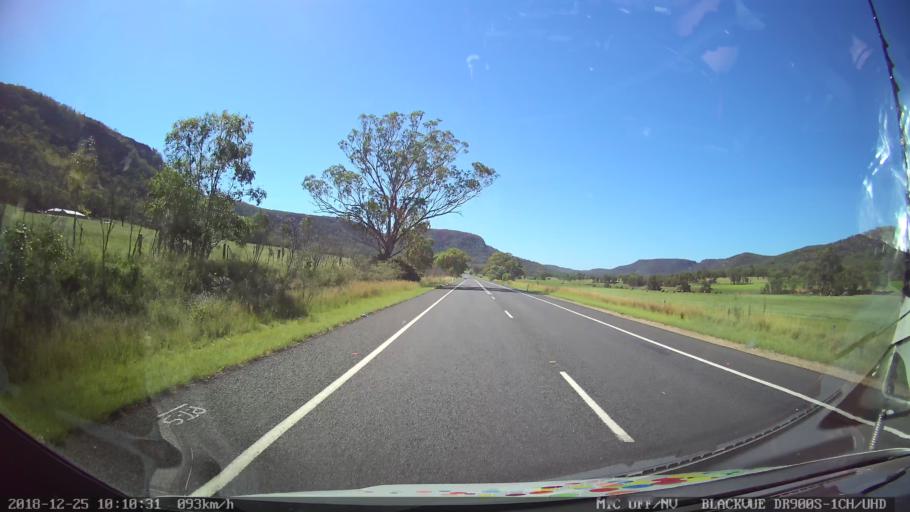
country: AU
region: New South Wales
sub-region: Muswellbrook
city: Denman
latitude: -32.3048
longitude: 150.5227
